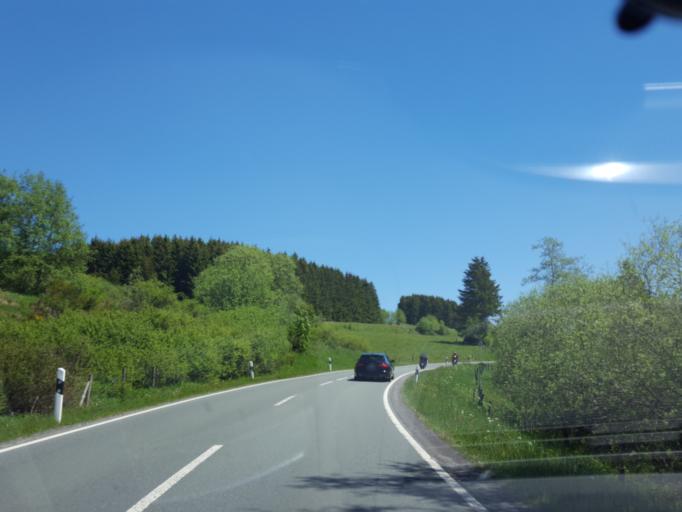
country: DE
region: North Rhine-Westphalia
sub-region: Regierungsbezirk Arnsberg
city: Winterberg
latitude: 51.2076
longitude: 8.5113
